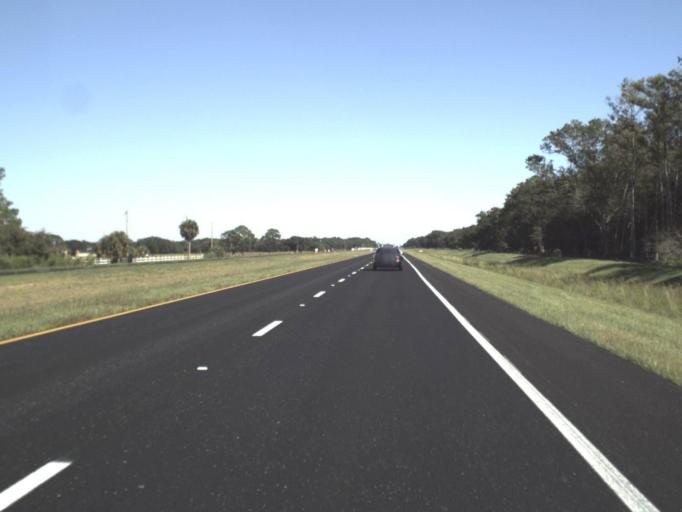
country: US
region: Florida
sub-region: Hendry County
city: Port LaBelle
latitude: 26.7683
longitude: -81.3477
